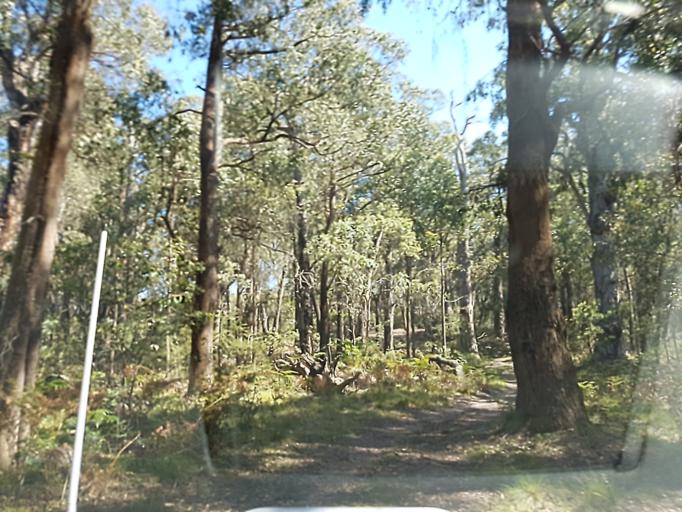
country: AU
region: Victoria
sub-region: East Gippsland
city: Lakes Entrance
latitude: -37.2219
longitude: 148.2821
